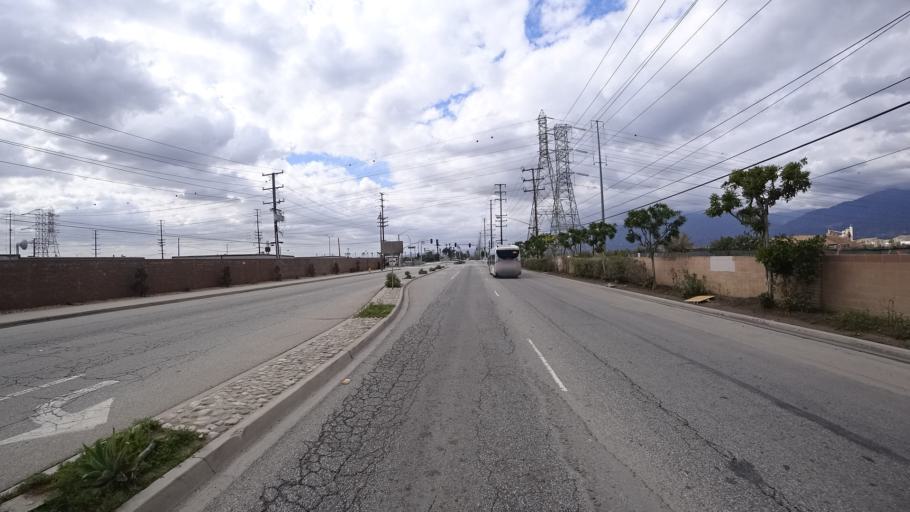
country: US
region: California
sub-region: Los Angeles County
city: Baldwin Park
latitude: 34.1082
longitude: -117.9784
